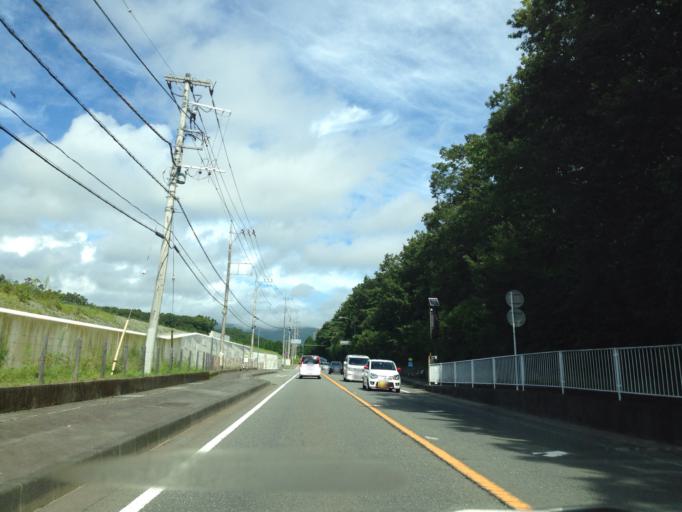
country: JP
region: Shizuoka
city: Gotemba
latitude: 35.3410
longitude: 138.8873
